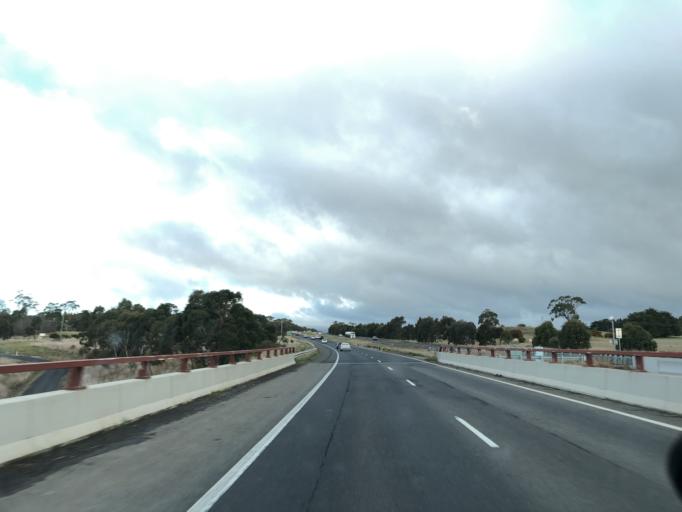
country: AU
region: Victoria
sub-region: Mount Alexander
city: Castlemaine
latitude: -37.2706
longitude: 144.4783
